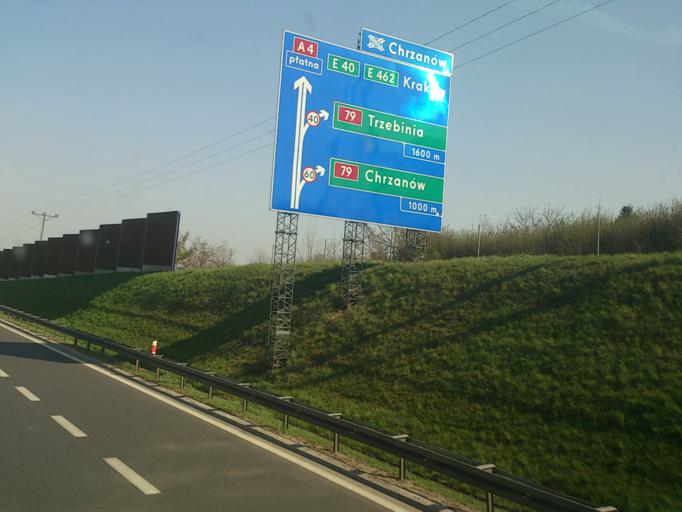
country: PL
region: Lesser Poland Voivodeship
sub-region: Powiat chrzanowski
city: Chrzanow
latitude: 50.1513
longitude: 19.4045
